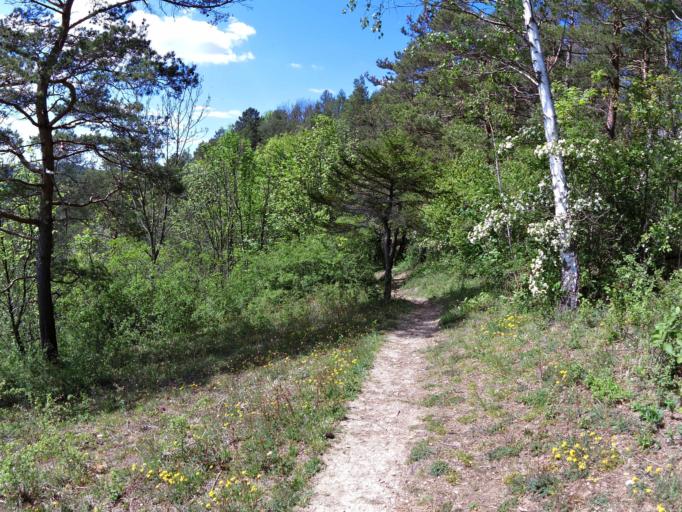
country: DE
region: Thuringia
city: Thal
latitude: 50.9678
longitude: 10.3719
